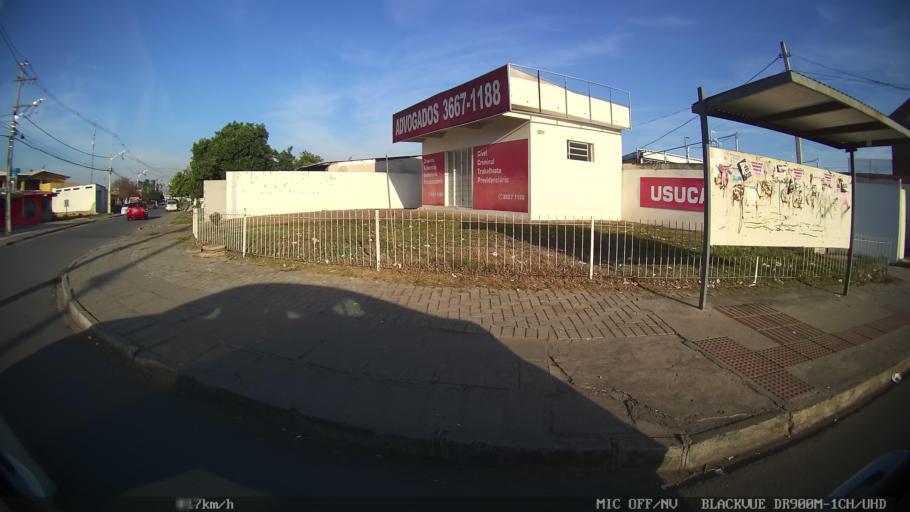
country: BR
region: Parana
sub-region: Pinhais
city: Pinhais
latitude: -25.4523
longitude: -49.1488
